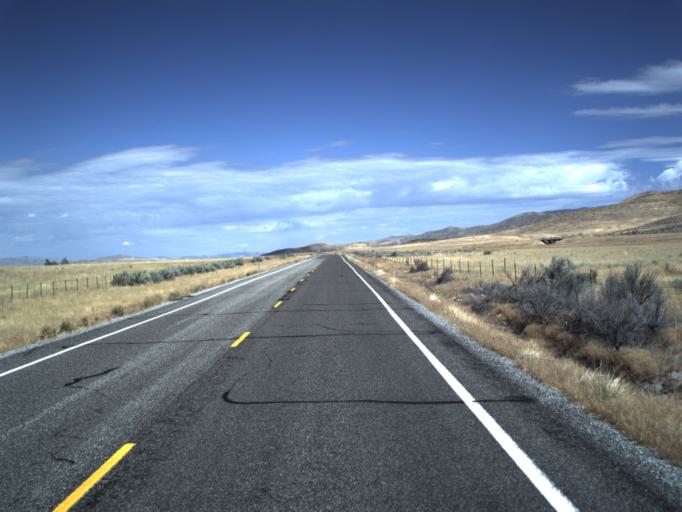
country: US
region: Utah
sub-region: Box Elder County
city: Garland
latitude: 41.8034
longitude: -112.4164
